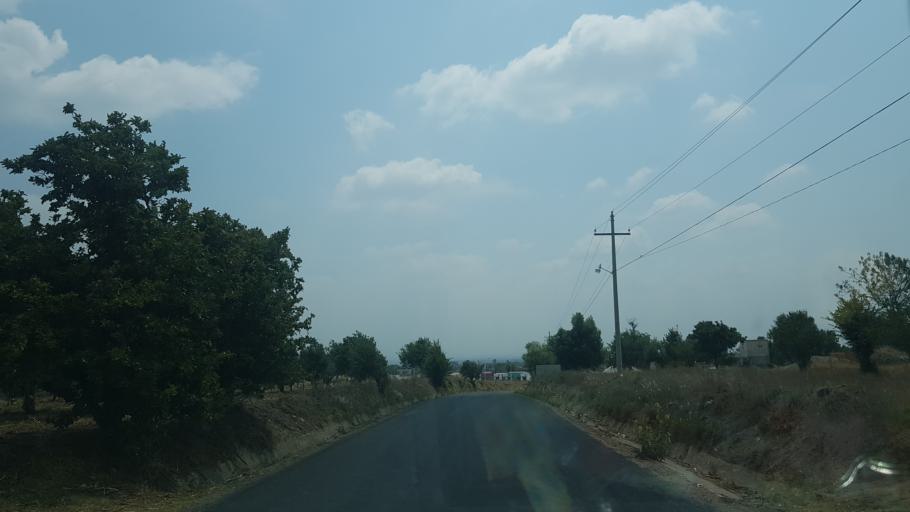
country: MX
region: Puebla
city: Huejotzingo
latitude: 19.1370
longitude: -98.4193
